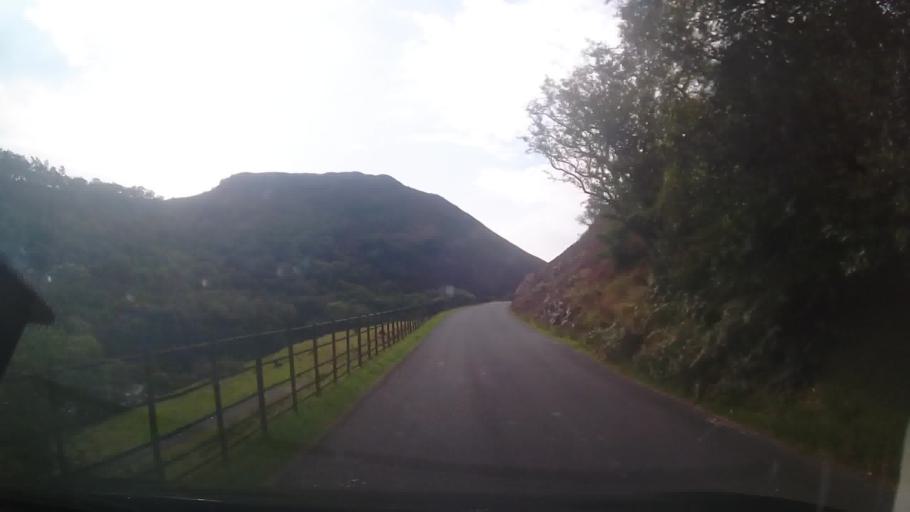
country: GB
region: Wales
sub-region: Sir Powys
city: Rhayader
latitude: 52.2718
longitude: -3.5701
